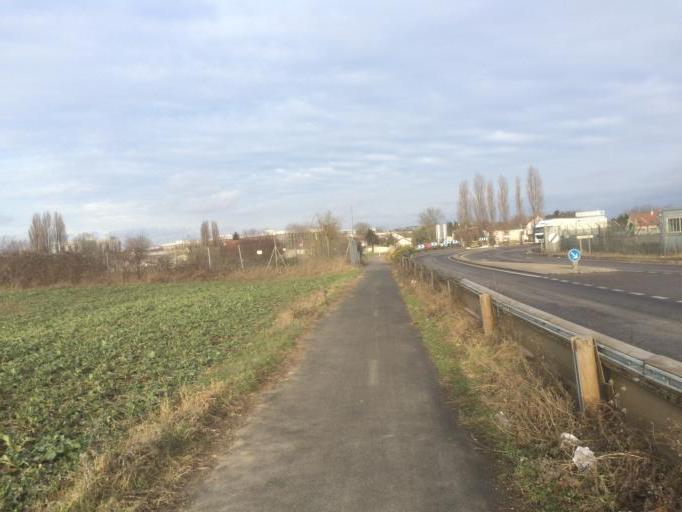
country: FR
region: Ile-de-France
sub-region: Departement du Val-de-Marne
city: Rungis
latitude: 48.7376
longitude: 2.3491
